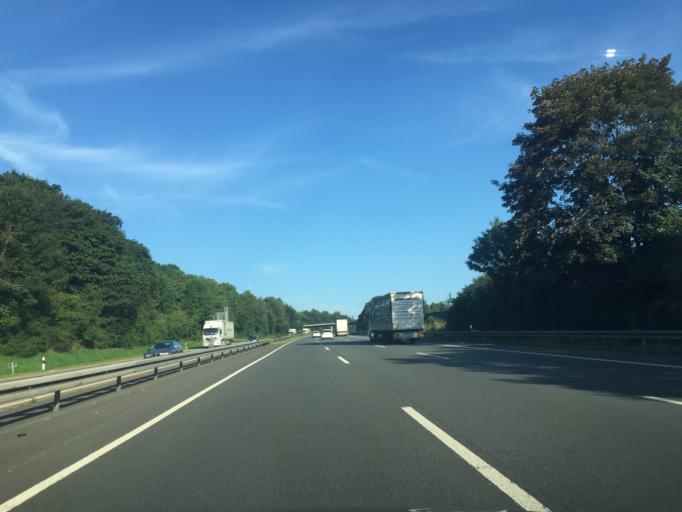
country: DE
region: North Rhine-Westphalia
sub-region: Regierungsbezirk Arnsberg
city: Olpe
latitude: 51.0370
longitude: 7.8118
